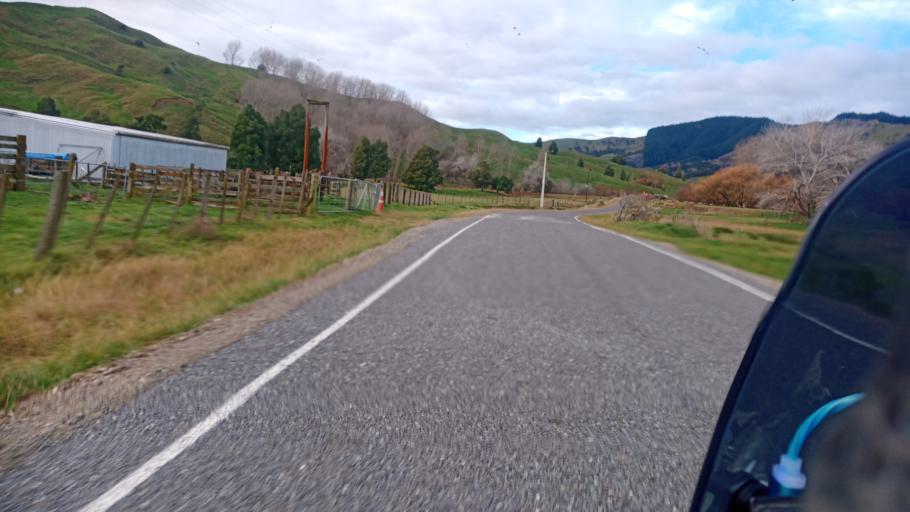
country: NZ
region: Gisborne
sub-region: Gisborne District
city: Gisborne
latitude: -38.4337
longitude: 177.8926
